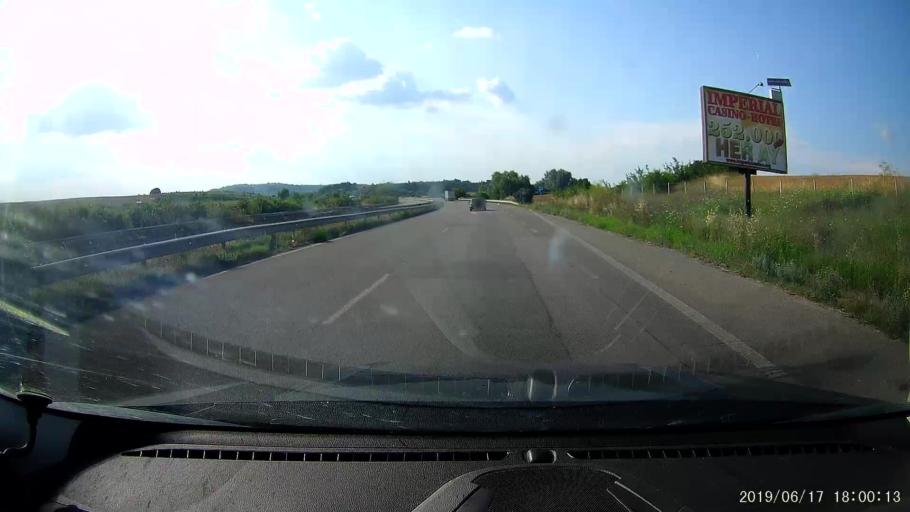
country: BG
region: Khaskovo
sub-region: Obshtina Svilengrad
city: Svilengrad
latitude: 41.7334
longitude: 26.2826
